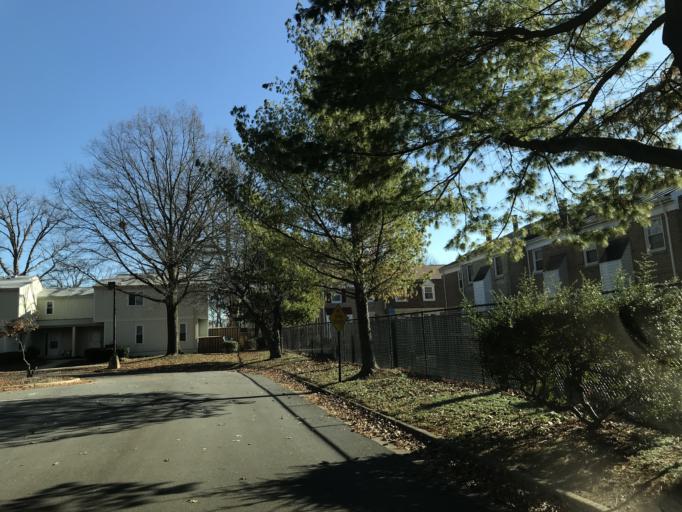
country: US
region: Virginia
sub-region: Fairfax County
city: Franconia
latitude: 38.7803
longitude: -77.1671
